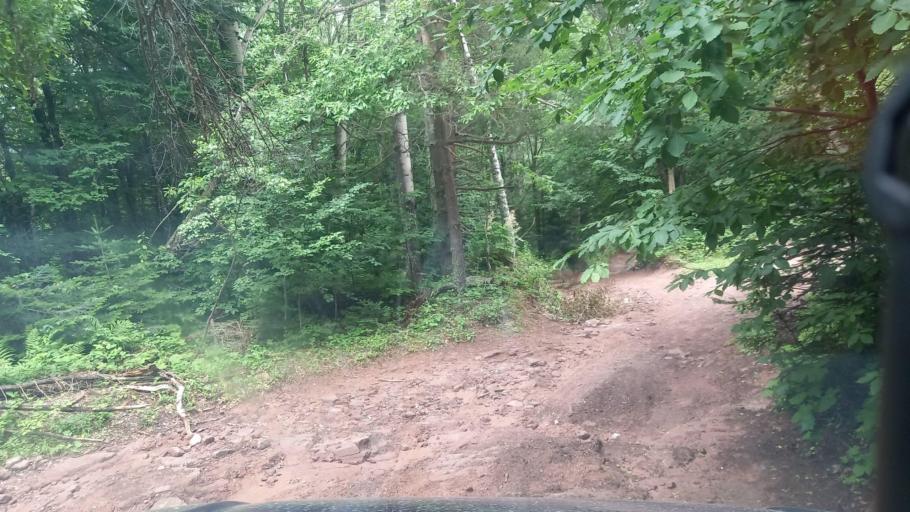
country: RU
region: Karachayevo-Cherkesiya
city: Kurdzhinovo
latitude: 43.8067
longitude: 40.8522
